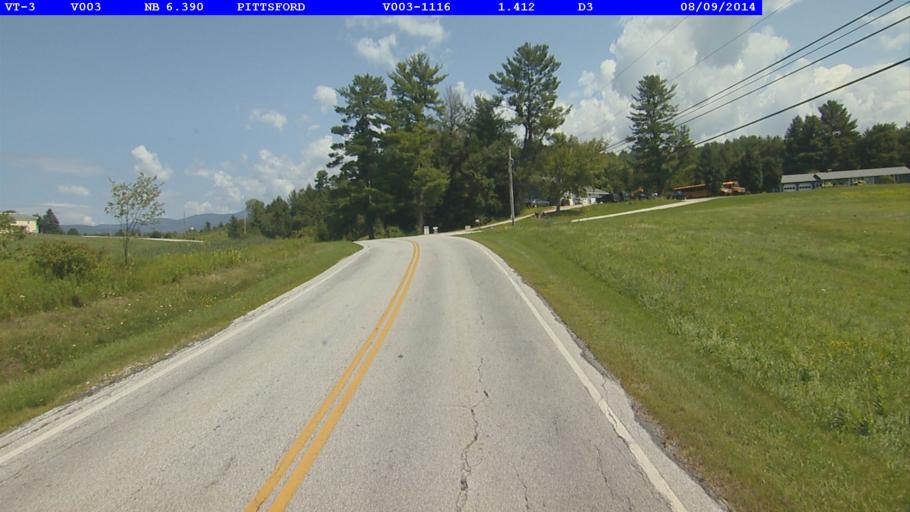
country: US
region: Vermont
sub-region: Rutland County
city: Rutland
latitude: 43.6836
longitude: -73.0221
